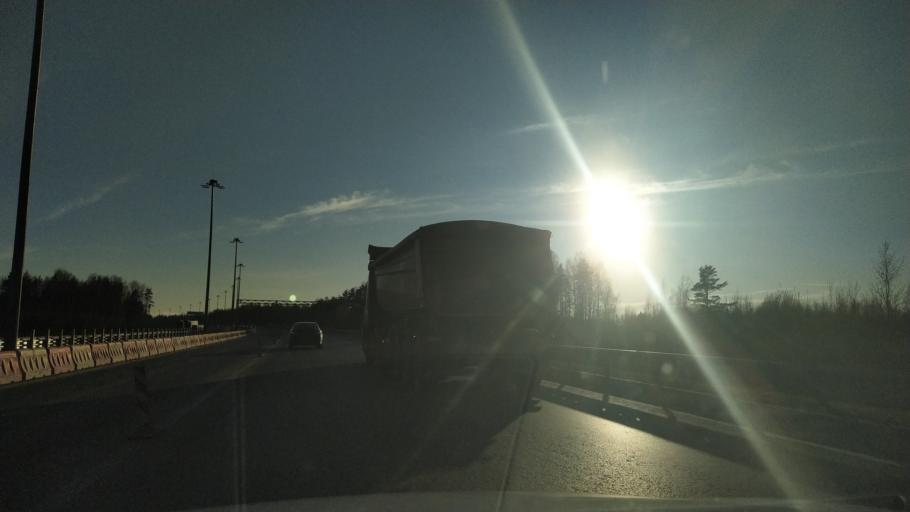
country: RU
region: St.-Petersburg
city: Levashovo
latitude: 60.0837
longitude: 30.2084
